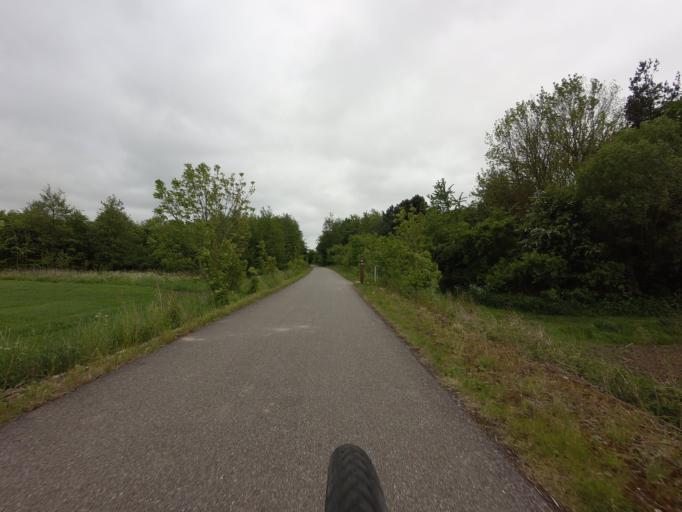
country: DK
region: Zealand
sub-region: Slagelse Kommune
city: Slagelse
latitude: 55.3001
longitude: 11.4153
